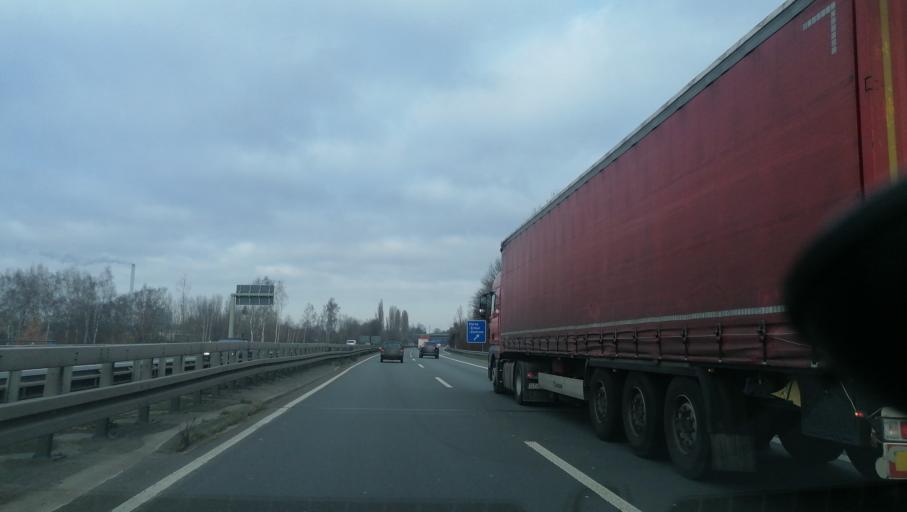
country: DE
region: North Rhine-Westphalia
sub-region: Regierungsbezirk Arnsberg
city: Herne
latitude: 51.5272
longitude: 7.2106
